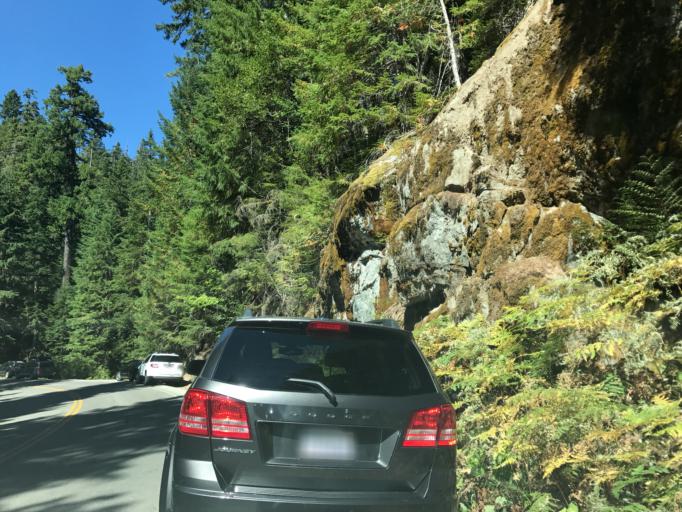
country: US
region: Washington
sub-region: Pierce County
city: Buckley
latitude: 46.7596
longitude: -121.5582
